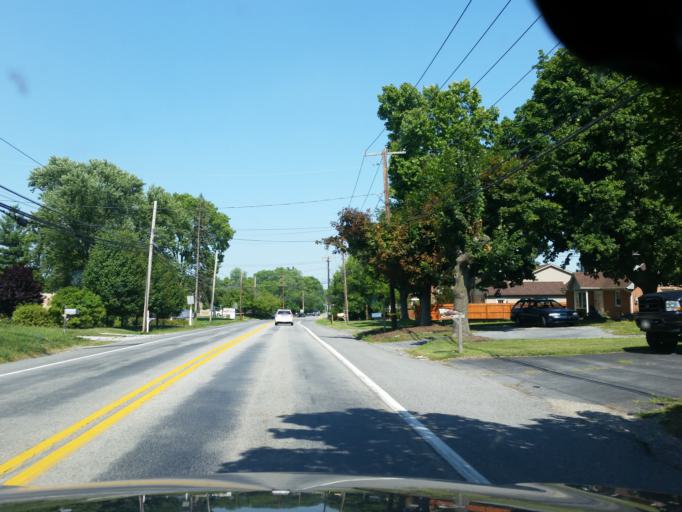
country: US
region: Pennsylvania
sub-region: Cumberland County
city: Mechanicsburg
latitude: 40.2066
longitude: -77.0317
